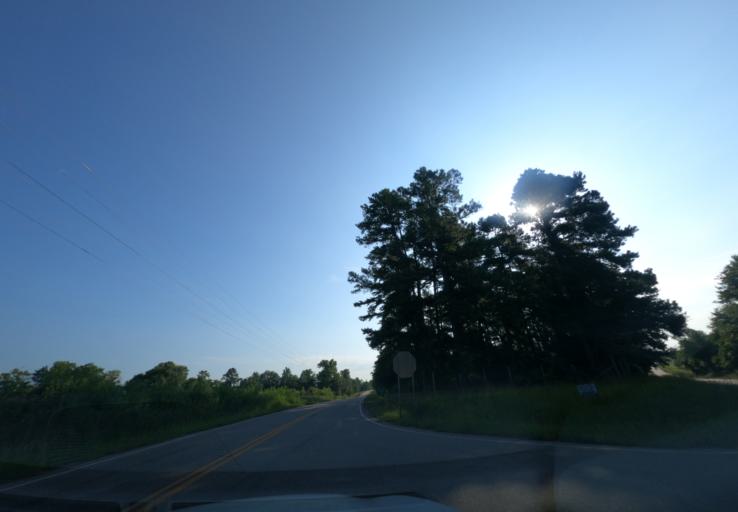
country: US
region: South Carolina
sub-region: Edgefield County
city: Murphys Estates
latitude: 33.6011
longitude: -81.9760
